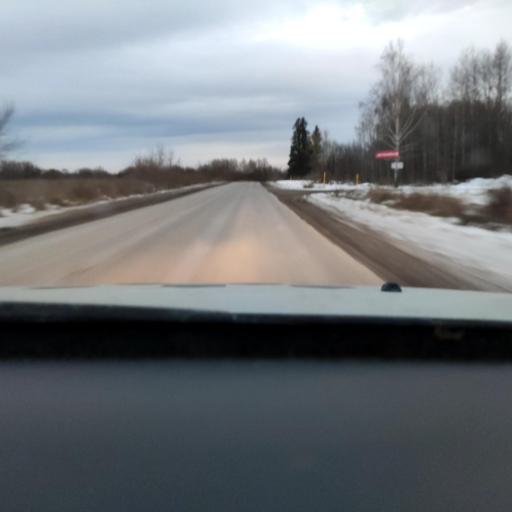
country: RU
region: Perm
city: Gamovo
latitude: 57.8999
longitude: 56.1200
